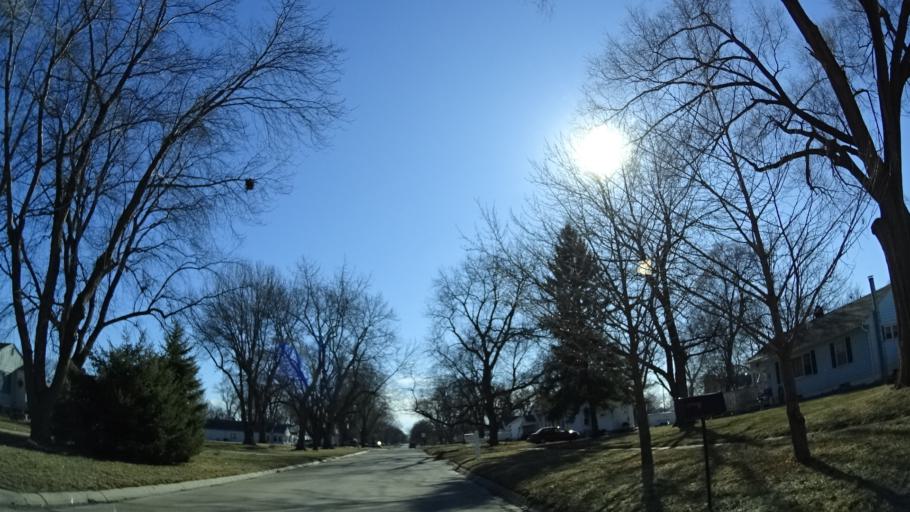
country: US
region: Nebraska
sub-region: Sarpy County
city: Bellevue
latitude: 41.1404
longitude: -95.8910
